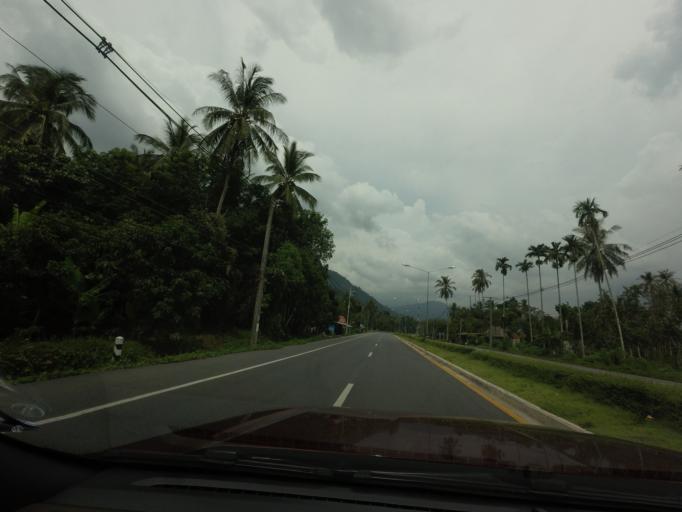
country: TH
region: Yala
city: Krong Pi Nang
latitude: 6.4704
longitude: 101.2681
